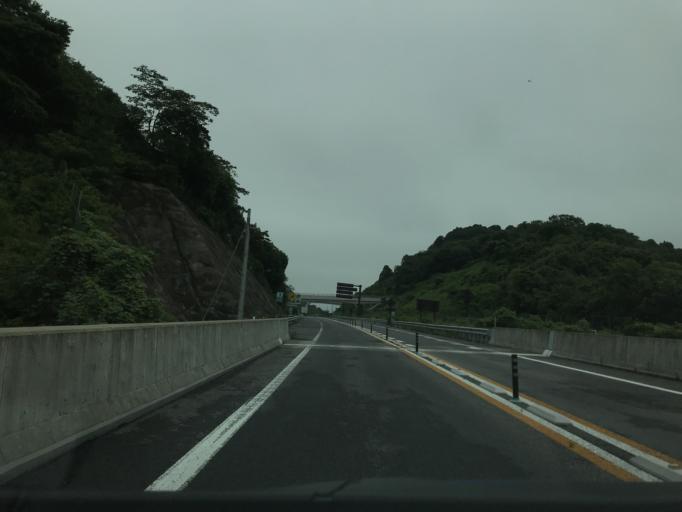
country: JP
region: Fukuoka
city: Nakatsu
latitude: 33.5041
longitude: 131.3016
